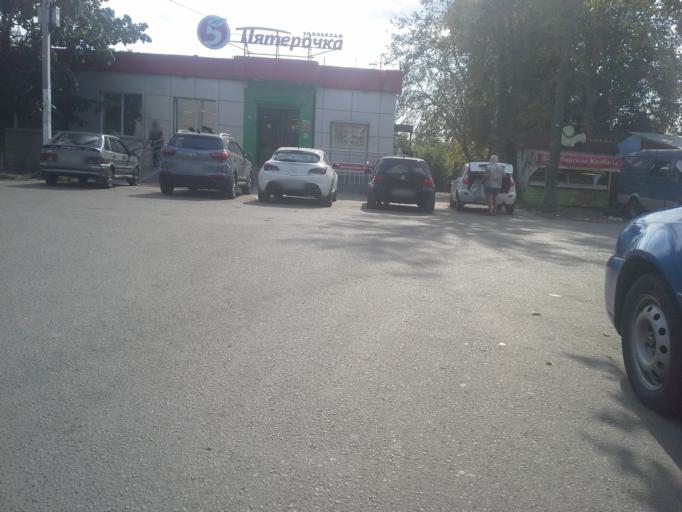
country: RU
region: Moskovskaya
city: Aprelevka
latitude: 55.5505
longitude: 37.0776
